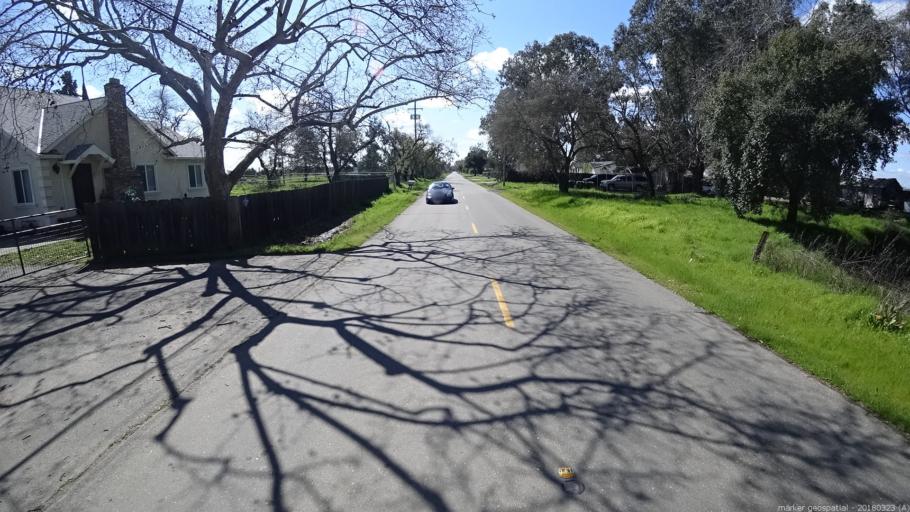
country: US
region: California
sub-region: Sacramento County
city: North Highlands
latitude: 38.6818
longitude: -121.4060
